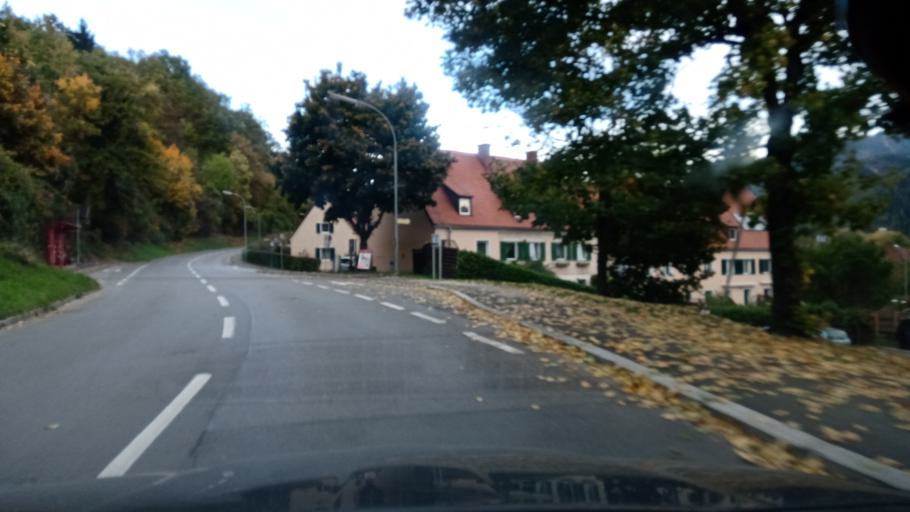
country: AT
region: Styria
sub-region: Politischer Bezirk Leoben
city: Proleb
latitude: 47.3886
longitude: 15.1139
